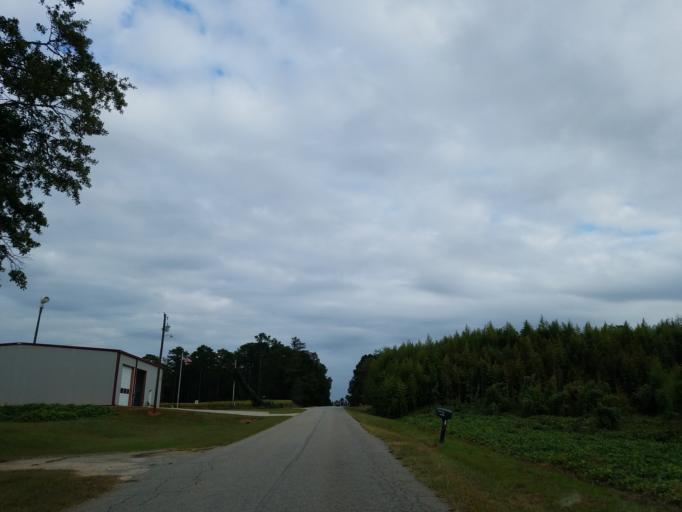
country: US
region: Georgia
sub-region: Lamar County
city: Barnesville
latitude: 33.1612
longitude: -84.0759
